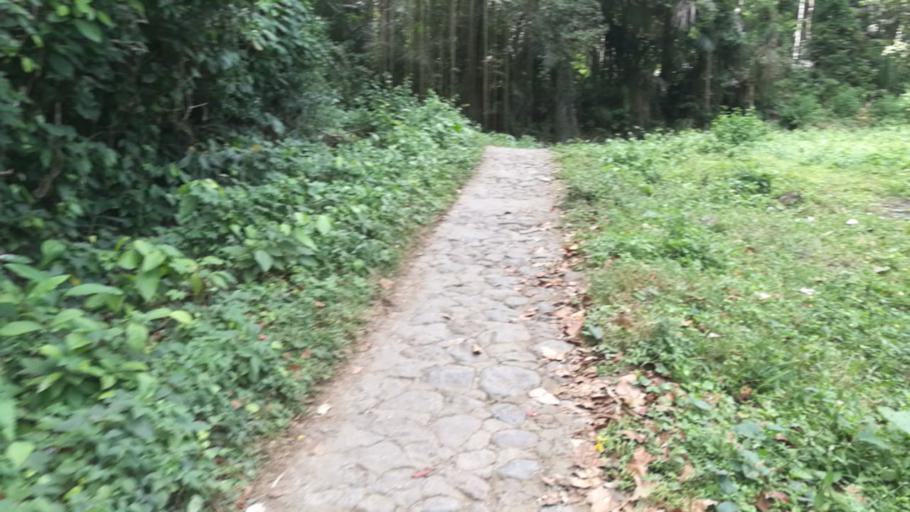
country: ID
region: Bali
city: Banjar Pegeringsingan
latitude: -8.4719
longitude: 115.5673
